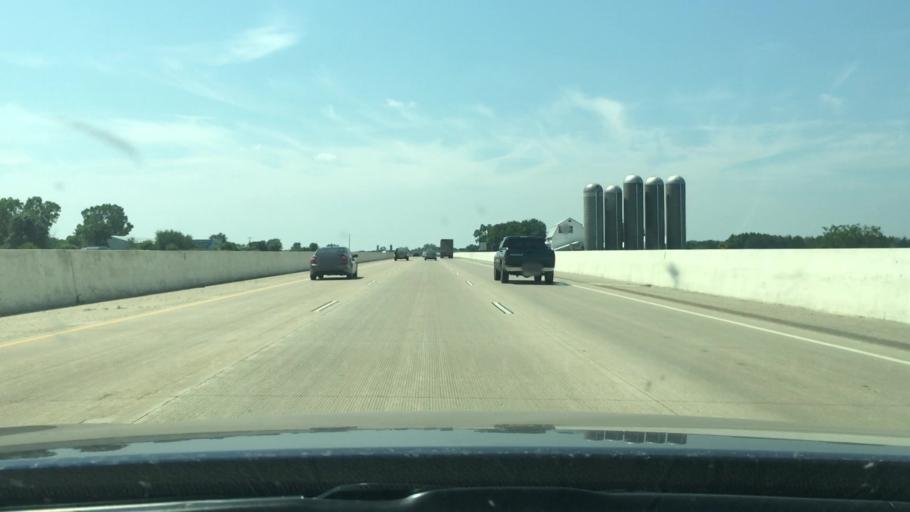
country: US
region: Wisconsin
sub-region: Winnebago County
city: Neenah
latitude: 44.1383
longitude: -88.4927
